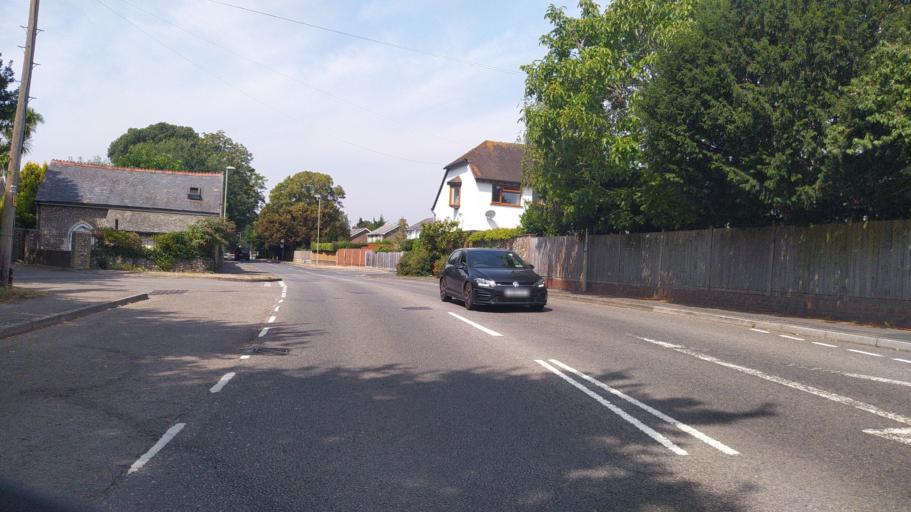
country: GB
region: England
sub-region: Hampshire
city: Havant
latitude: 50.8497
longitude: -0.9661
